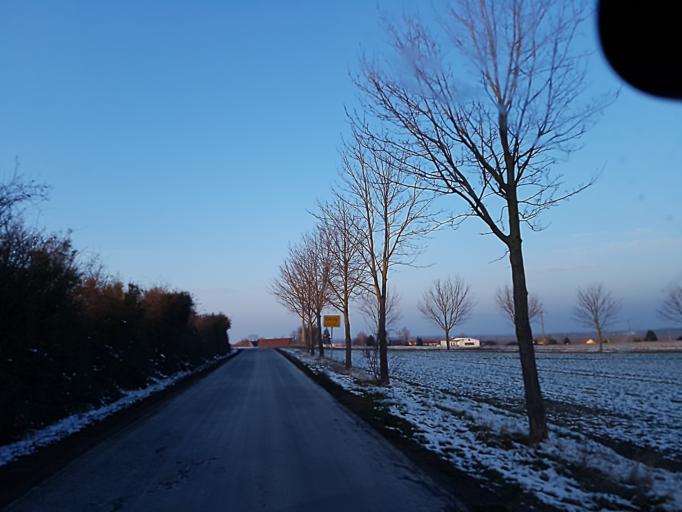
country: DE
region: Saxony
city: Strehla
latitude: 51.3676
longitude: 13.2242
